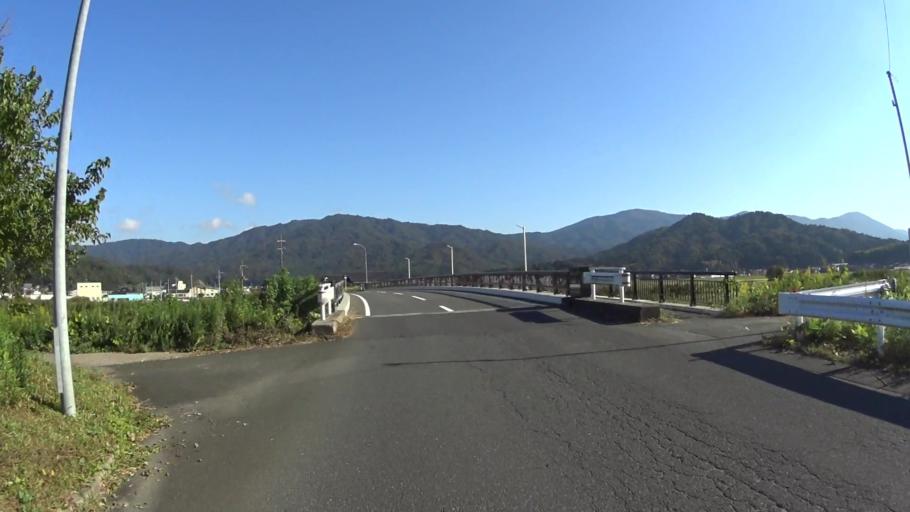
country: JP
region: Kyoto
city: Miyazu
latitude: 35.5333
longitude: 135.1157
